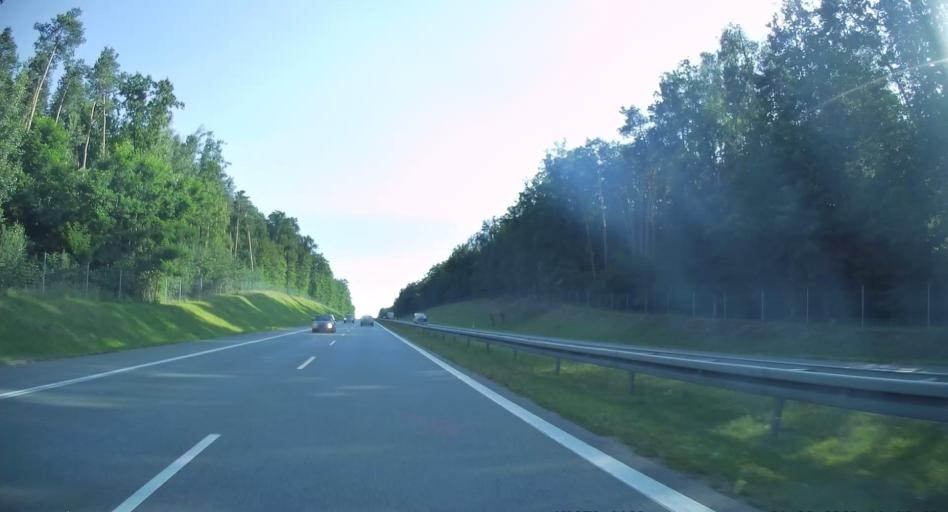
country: PL
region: Masovian Voivodeship
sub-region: Powiat bialobrzeski
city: Bialobrzegi
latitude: 51.6419
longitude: 20.9736
